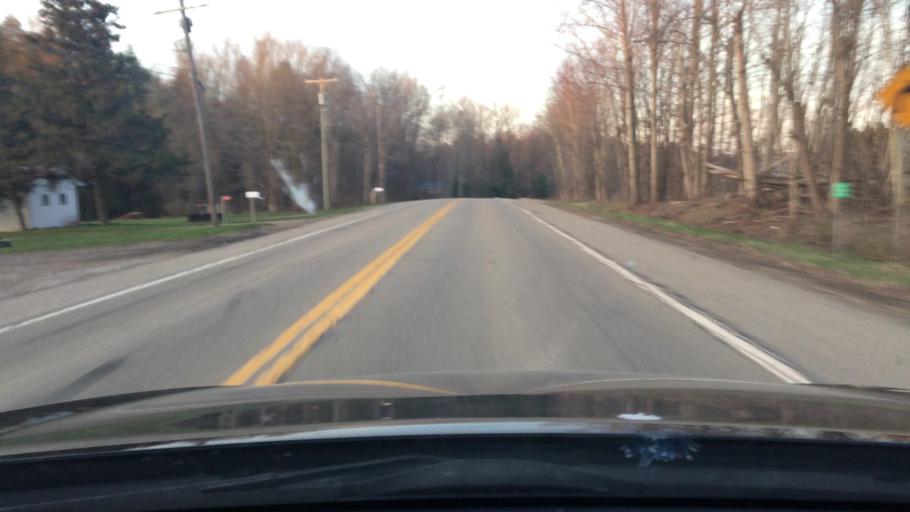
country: US
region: New York
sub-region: Cattaraugus County
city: Randolph
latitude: 42.1868
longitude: -78.9159
